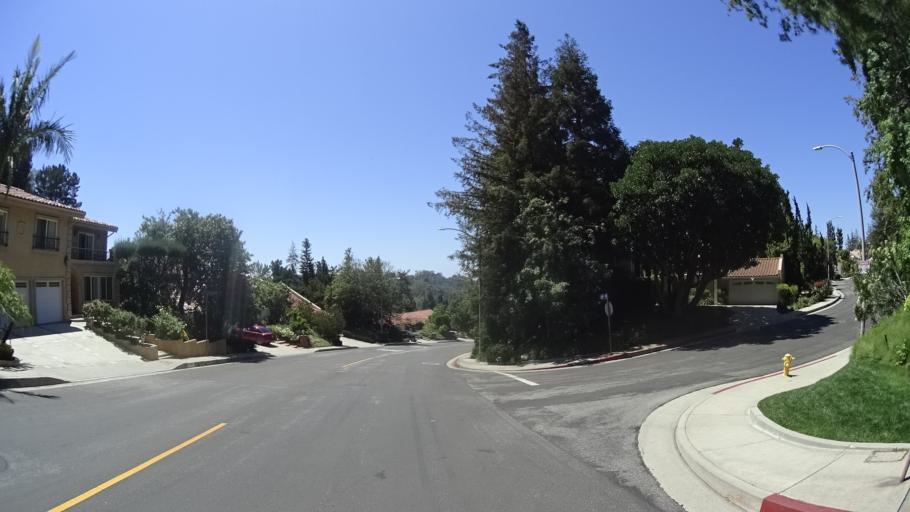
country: US
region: California
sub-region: Los Angeles County
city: Sherman Oaks
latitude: 34.1274
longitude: -118.4476
